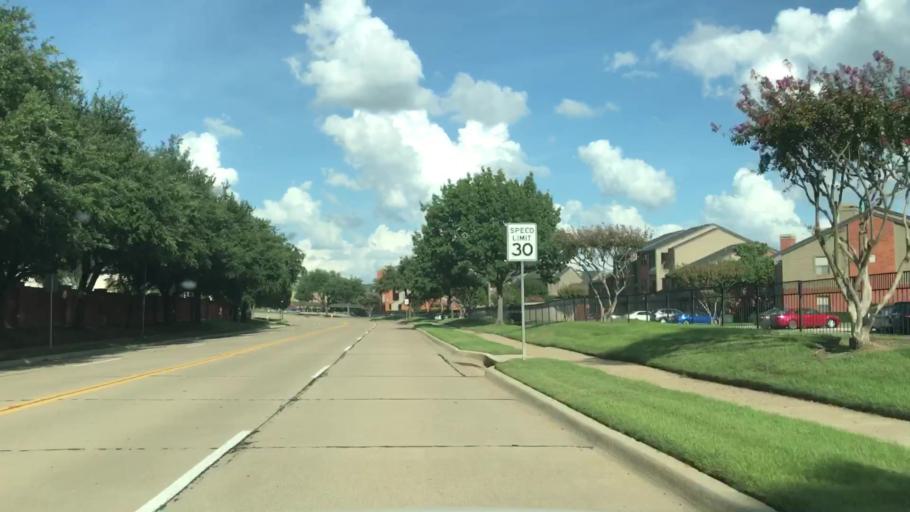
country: US
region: Texas
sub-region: Dallas County
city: Coppell
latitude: 32.9401
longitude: -96.9577
